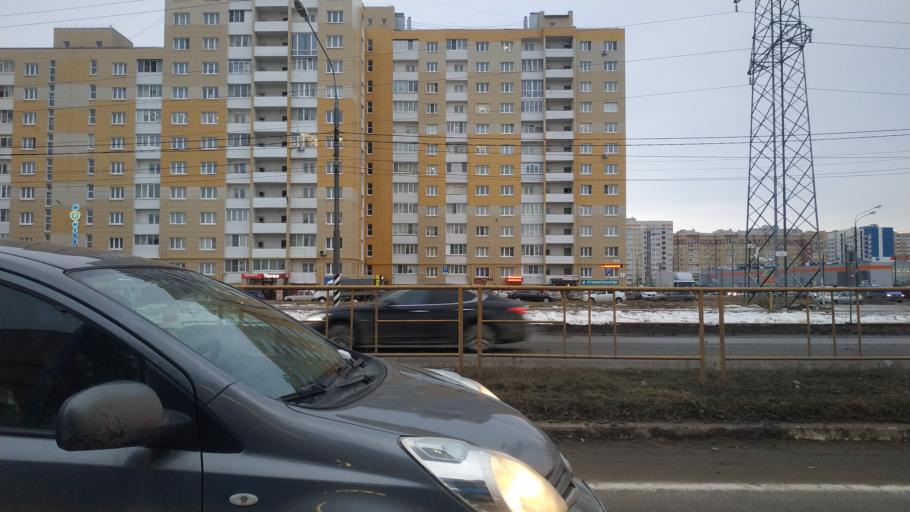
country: RU
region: Tverskaya
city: Tver
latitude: 56.8186
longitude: 35.8849
